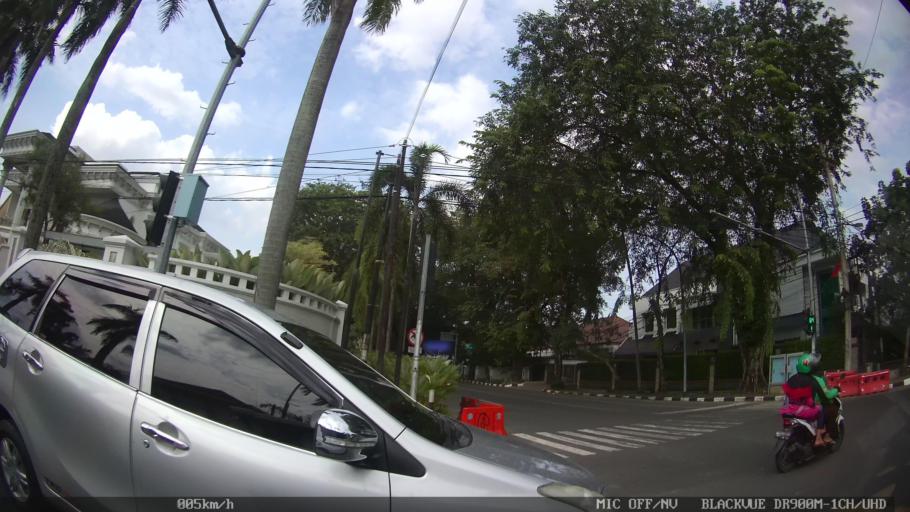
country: ID
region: North Sumatra
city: Medan
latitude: 3.5737
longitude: 98.6710
